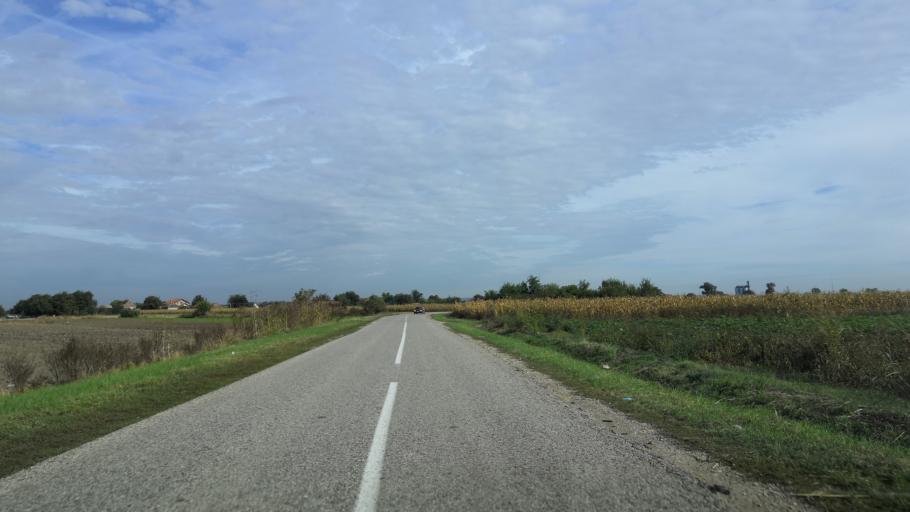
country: RS
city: Novi Karlovci
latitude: 45.0626
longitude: 20.1800
